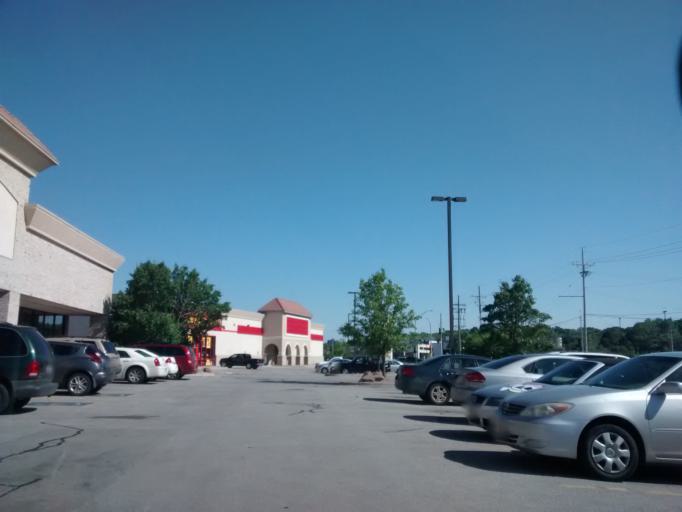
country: US
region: Nebraska
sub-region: Douglas County
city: Ralston
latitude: 41.2612
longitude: -96.0358
